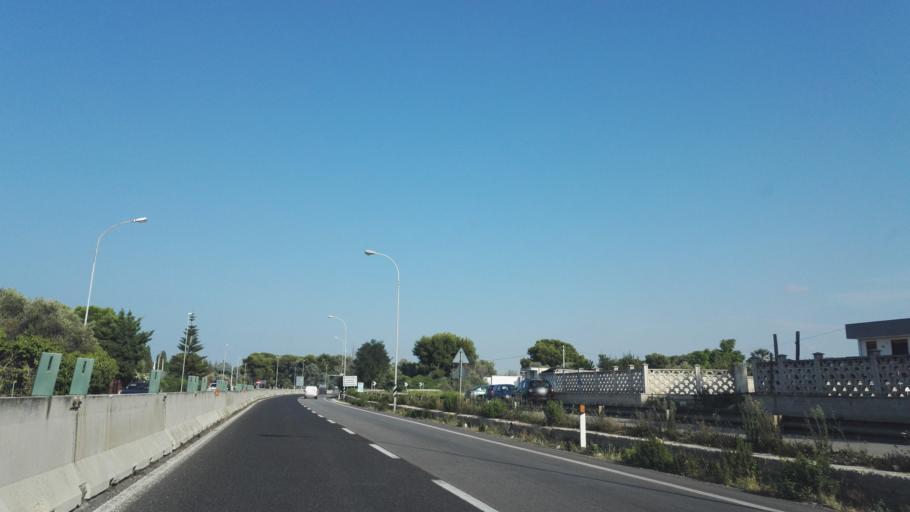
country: IT
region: Apulia
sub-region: Provincia di Bari
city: Parco Scizzo-Parchitello
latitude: 41.0876
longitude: 16.9858
